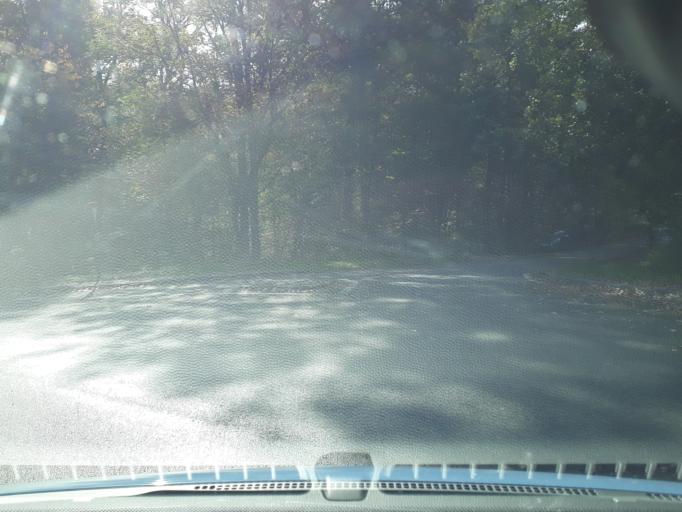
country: FR
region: Ile-de-France
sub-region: Departement de Seine-et-Marne
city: Bois-le-Roi
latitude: 48.4664
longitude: 2.6897
